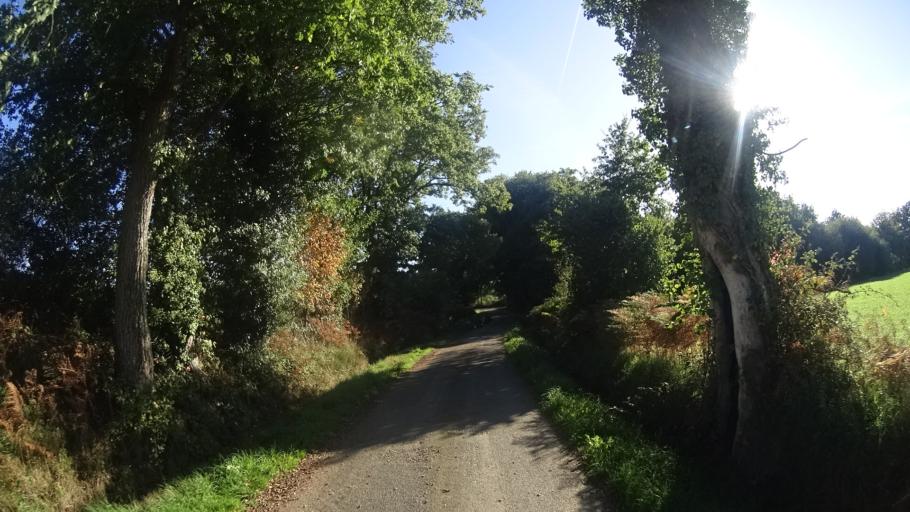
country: FR
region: Brittany
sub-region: Departement du Morbihan
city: Saint-Vincent-sur-Oust
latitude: 47.6979
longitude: -2.1806
